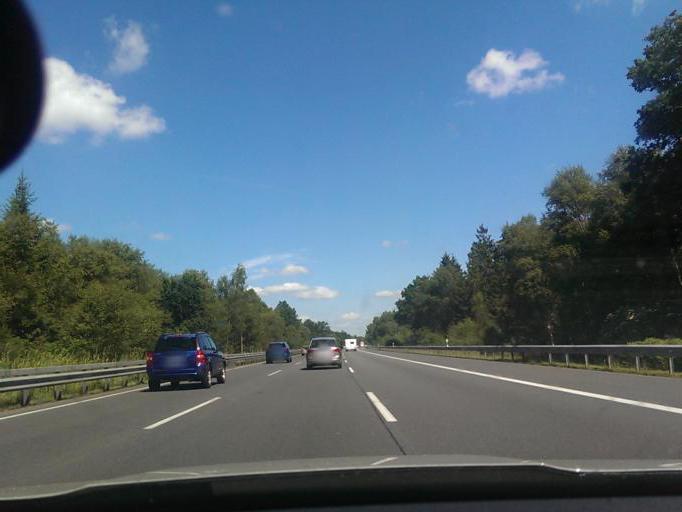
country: DE
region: Lower Saxony
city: Hademstorf
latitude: 52.7486
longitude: 9.6674
